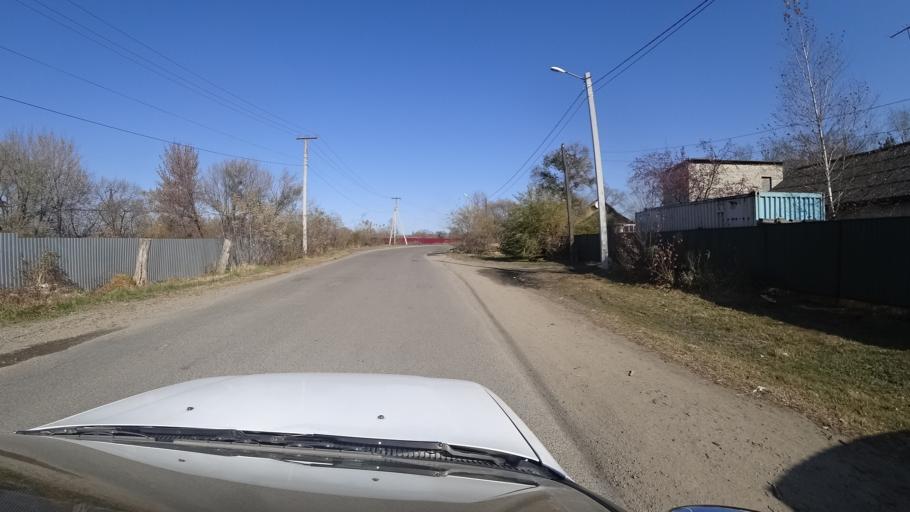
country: RU
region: Primorskiy
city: Dal'nerechensk
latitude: 45.9323
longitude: 133.7487
